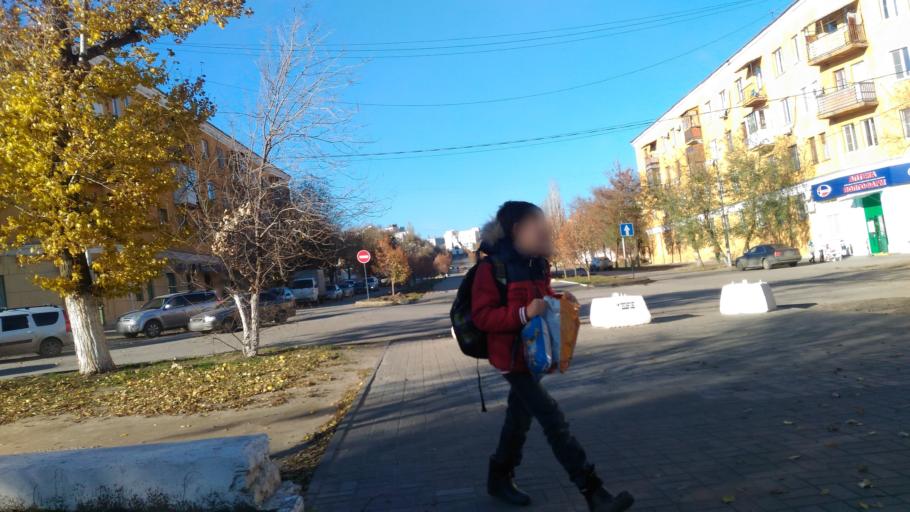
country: RU
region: Volgograd
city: Volgograd
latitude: 48.6597
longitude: 44.4458
